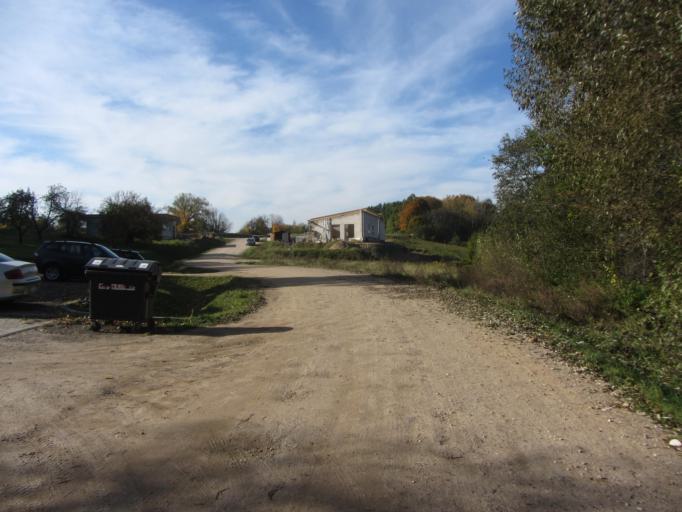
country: LT
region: Vilnius County
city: Elektrenai
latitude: 54.7820
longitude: 24.6900
